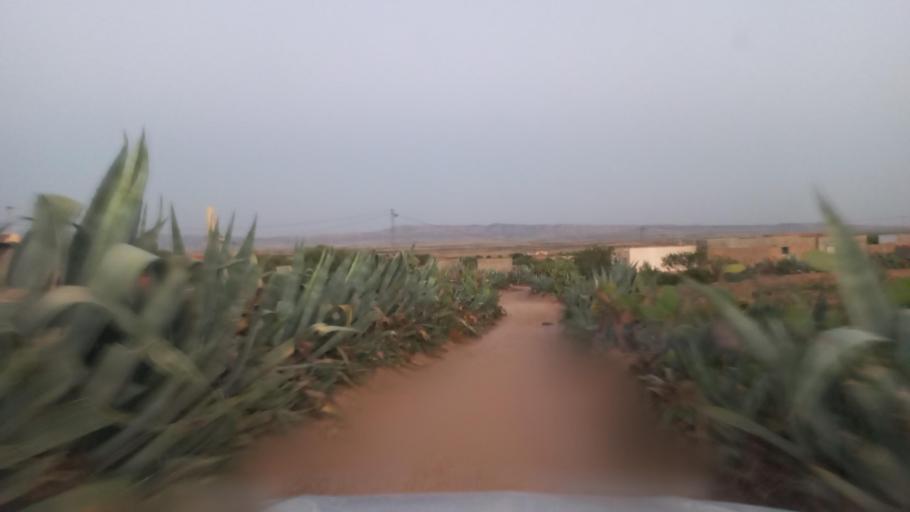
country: TN
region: Al Qasrayn
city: Sbiba
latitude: 35.3776
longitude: 9.0144
